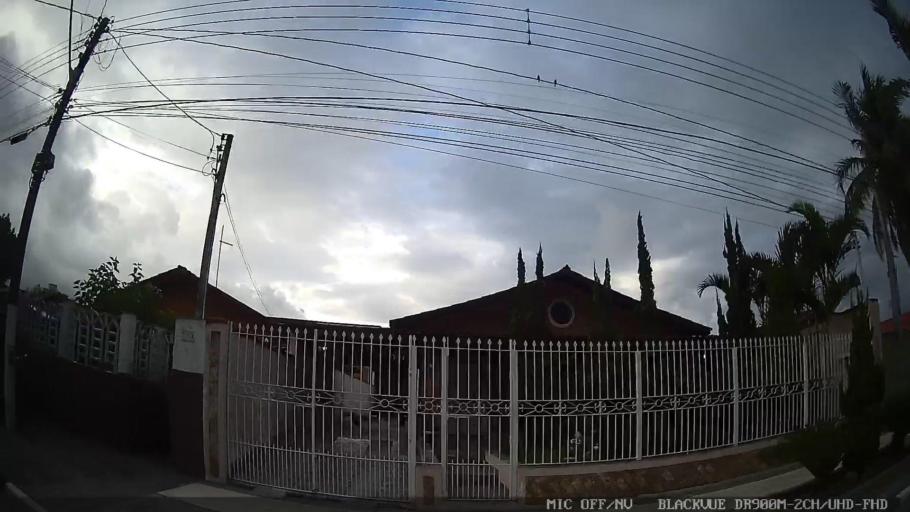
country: BR
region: Sao Paulo
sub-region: Caraguatatuba
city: Caraguatatuba
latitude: -23.6285
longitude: -45.4220
